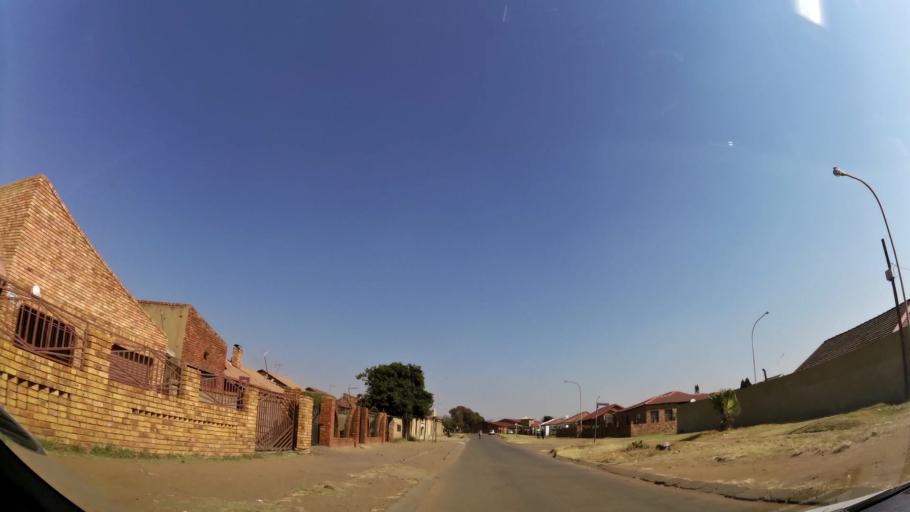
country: ZA
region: Gauteng
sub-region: Ekurhuleni Metropolitan Municipality
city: Benoni
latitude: -26.2215
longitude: 28.3040
